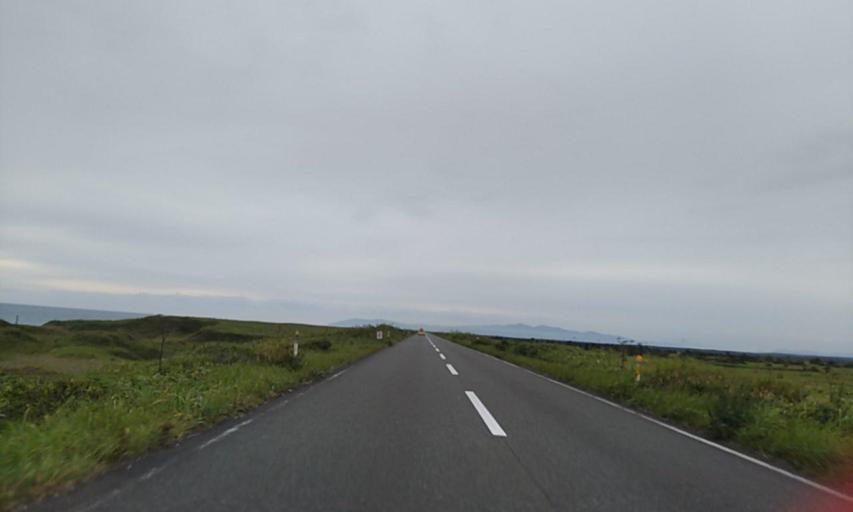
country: JP
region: Hokkaido
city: Makubetsu
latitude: 45.2679
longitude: 142.2392
